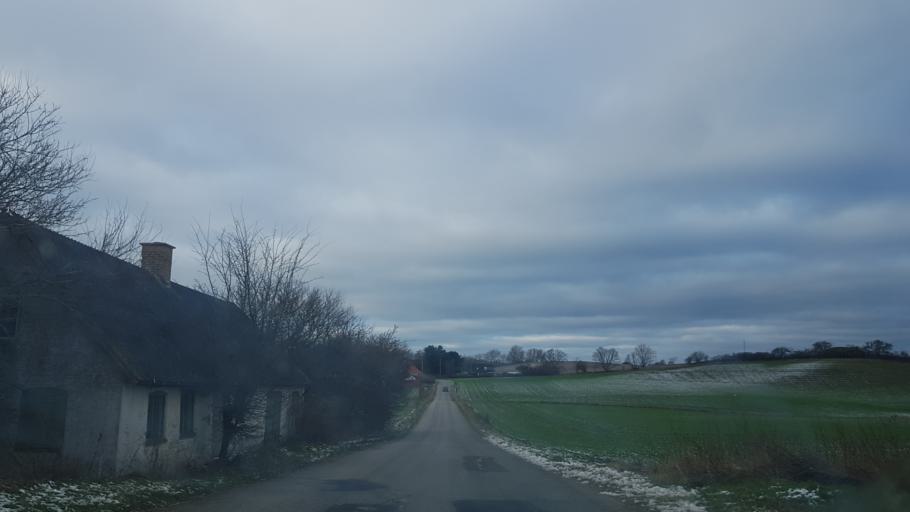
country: DK
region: Zealand
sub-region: Odsherred Kommune
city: Hojby
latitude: 55.9251
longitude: 11.5597
